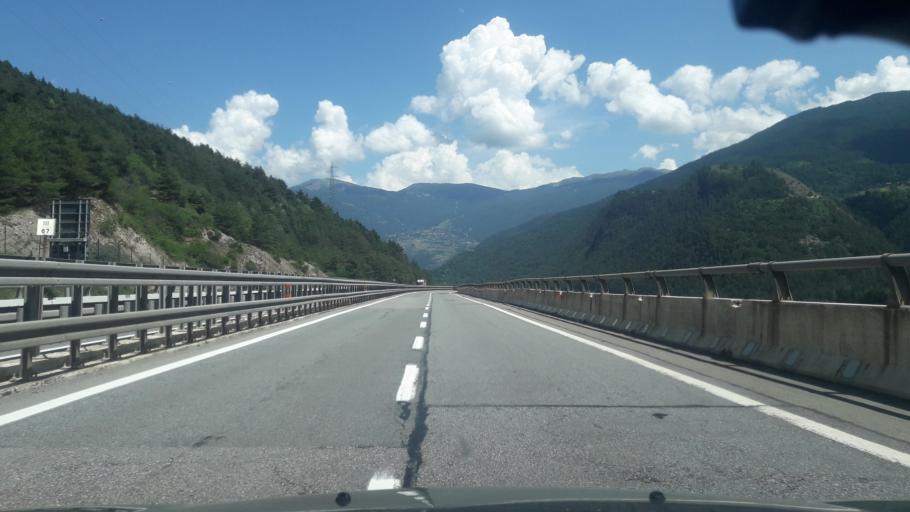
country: IT
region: Piedmont
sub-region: Provincia di Torino
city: Bardonecchia
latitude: 45.0486
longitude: 6.7553
